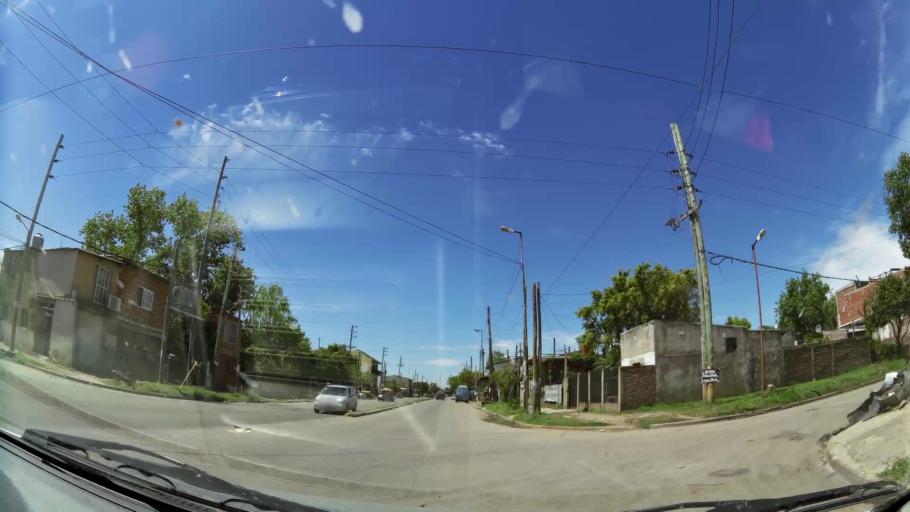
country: AR
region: Buenos Aires
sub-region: Partido de Quilmes
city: Quilmes
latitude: -34.7336
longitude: -58.3093
